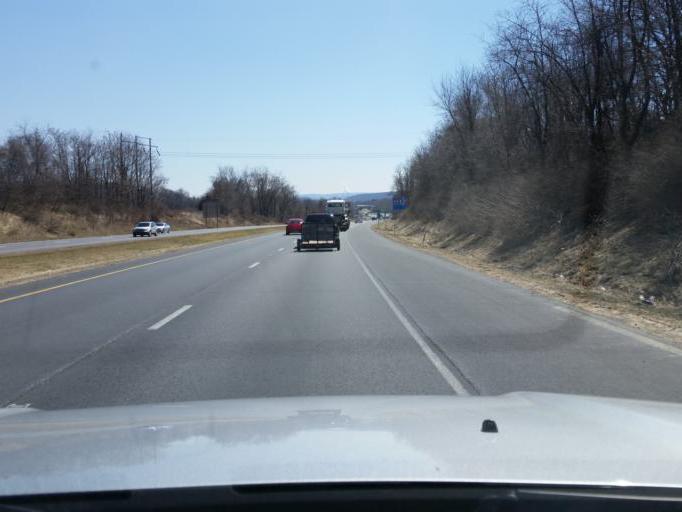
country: US
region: Pennsylvania
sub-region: Dauphin County
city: Bressler
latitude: 40.2345
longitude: -76.7980
